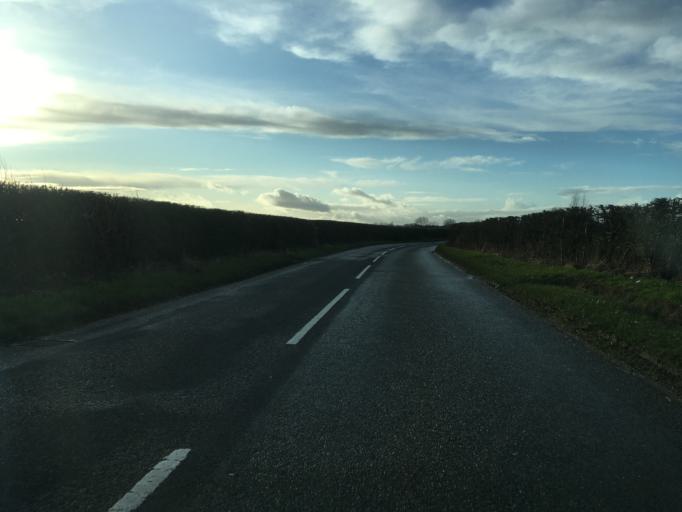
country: GB
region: England
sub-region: Warwickshire
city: Stratford-upon-Avon
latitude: 52.2243
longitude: -1.7489
